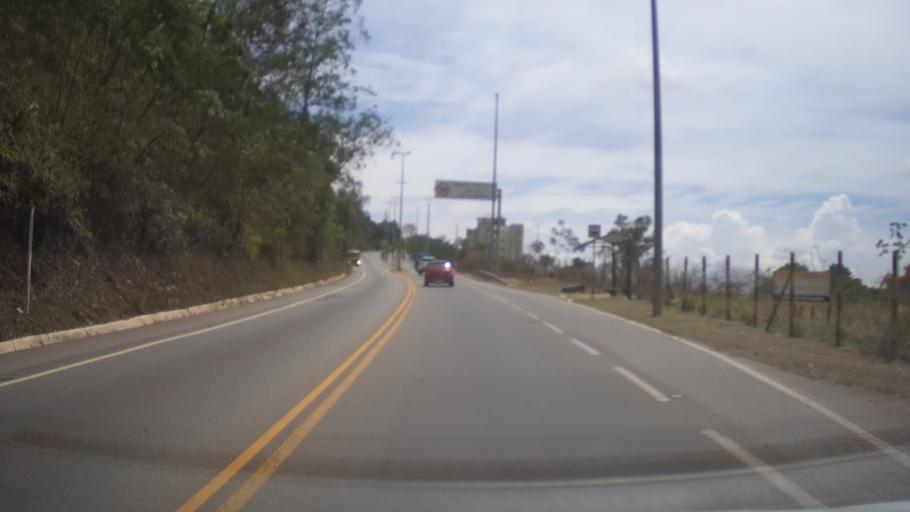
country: BR
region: Minas Gerais
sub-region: Nova Lima
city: Nova Lima
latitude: -19.9974
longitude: -43.8587
